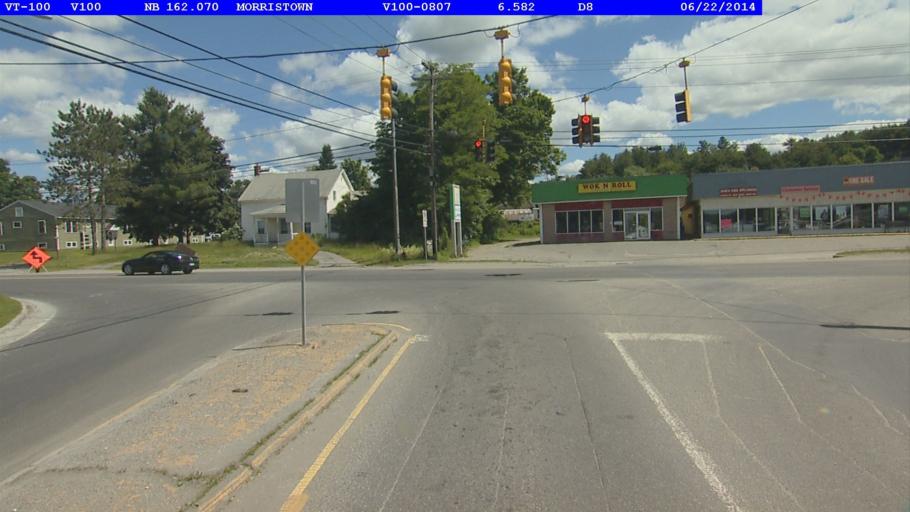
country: US
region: Vermont
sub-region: Lamoille County
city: Morrisville
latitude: 44.5755
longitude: -72.5926
